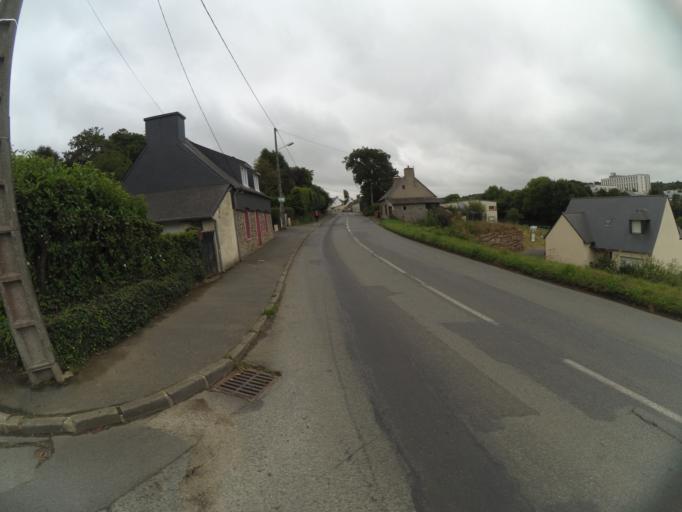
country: FR
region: Brittany
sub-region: Departement des Cotes-d'Armor
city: Lannion
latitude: 48.7240
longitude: -3.4599
